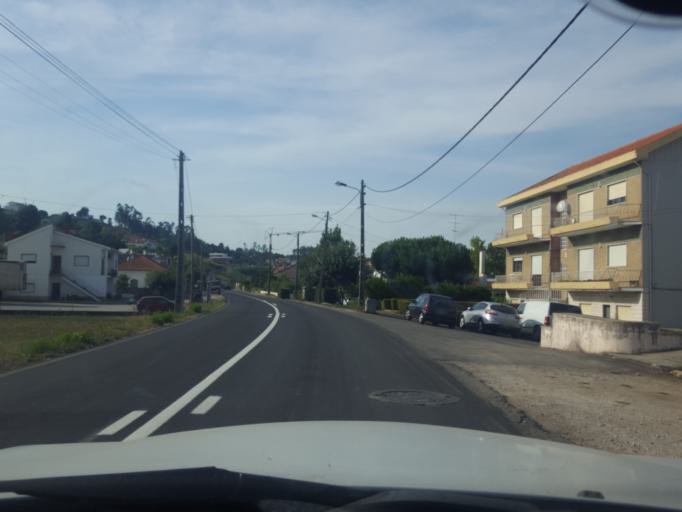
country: PT
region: Leiria
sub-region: Leiria
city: Leiria
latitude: 39.7006
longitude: -8.7894
